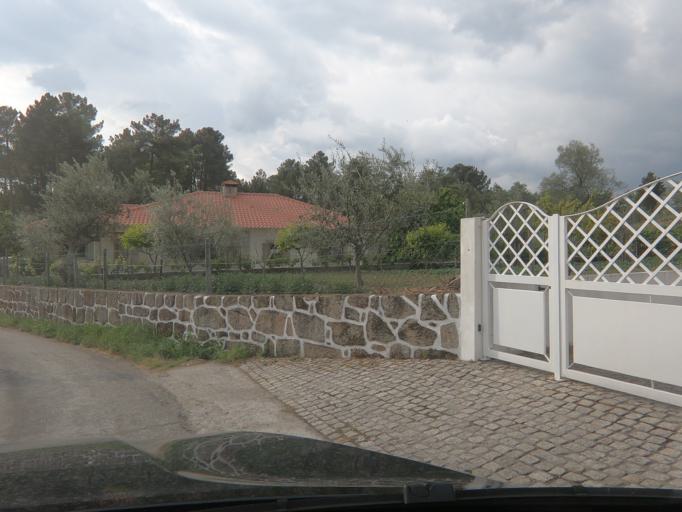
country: PT
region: Vila Real
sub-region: Vila Real
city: Vila Real
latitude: 41.3095
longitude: -7.7011
